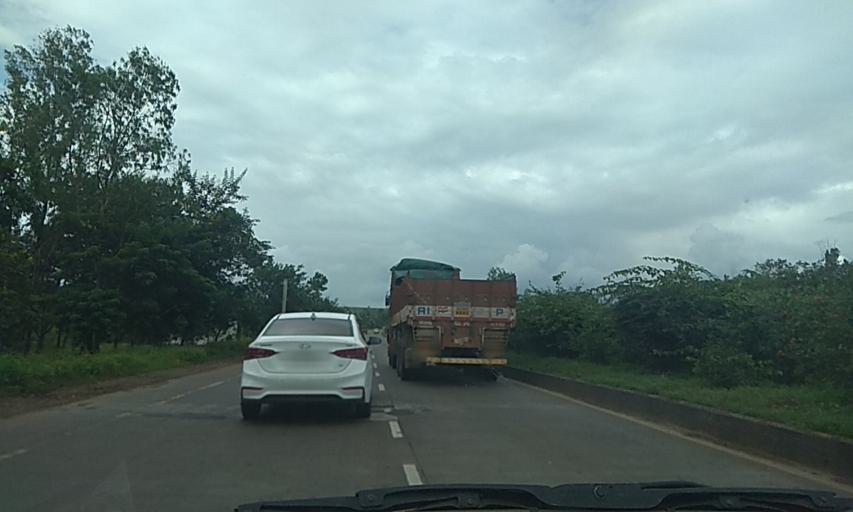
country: IN
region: Maharashtra
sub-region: Kolhapur
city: Kagal
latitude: 16.5908
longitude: 74.3079
